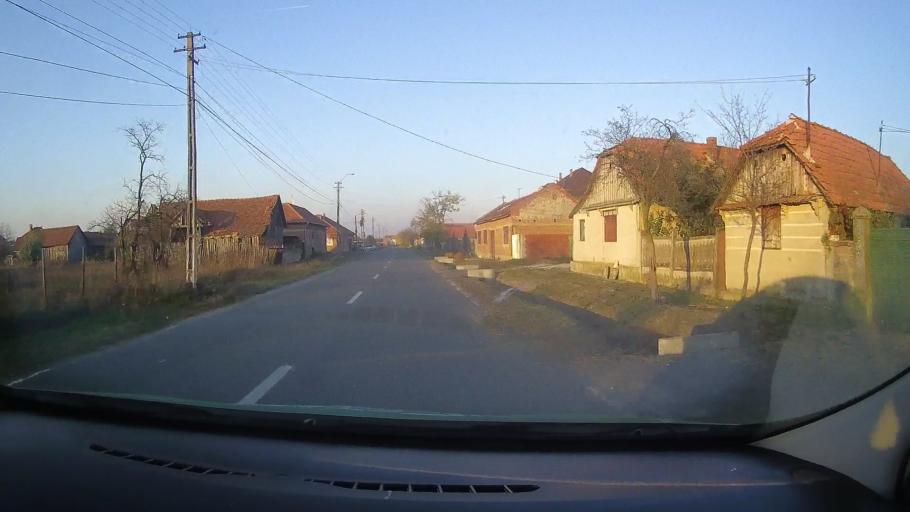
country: RO
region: Timis
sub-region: Comuna Traian Vuia
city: Traian Vuia
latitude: 45.8021
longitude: 22.0245
